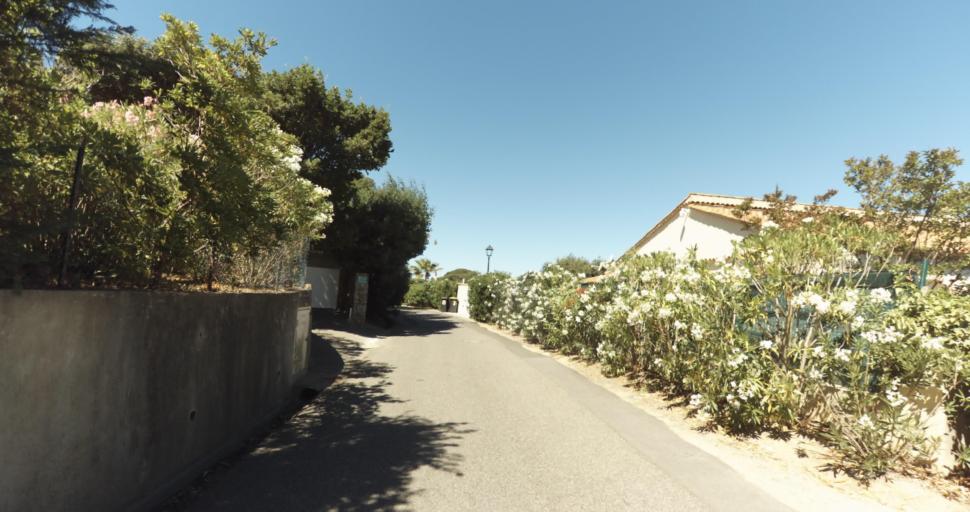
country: FR
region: Provence-Alpes-Cote d'Azur
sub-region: Departement du Var
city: Gassin
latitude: 43.2611
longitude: 6.6012
